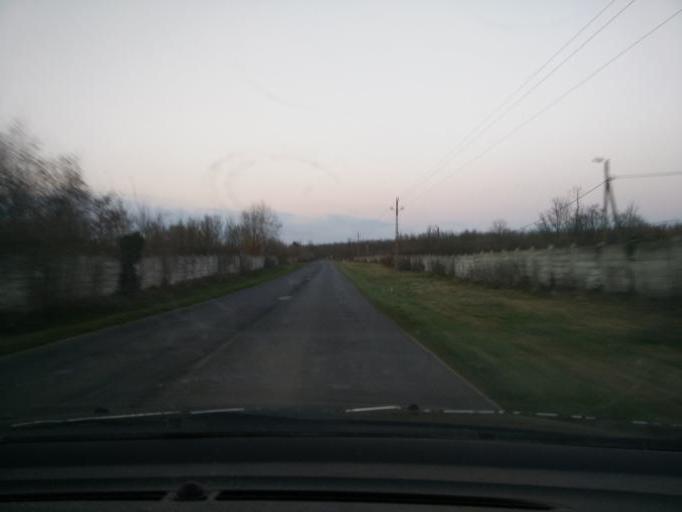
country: HU
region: Veszprem
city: Devecser
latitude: 47.0847
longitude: 17.4068
